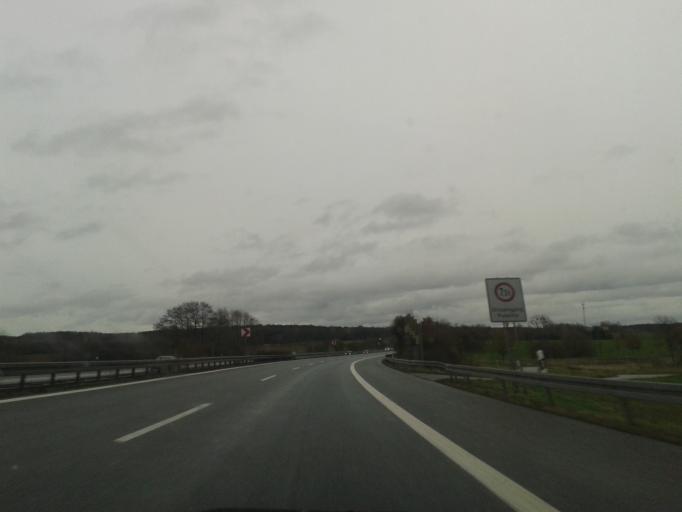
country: DE
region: Saxony
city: Lichtenberg
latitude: 51.1605
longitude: 13.9622
